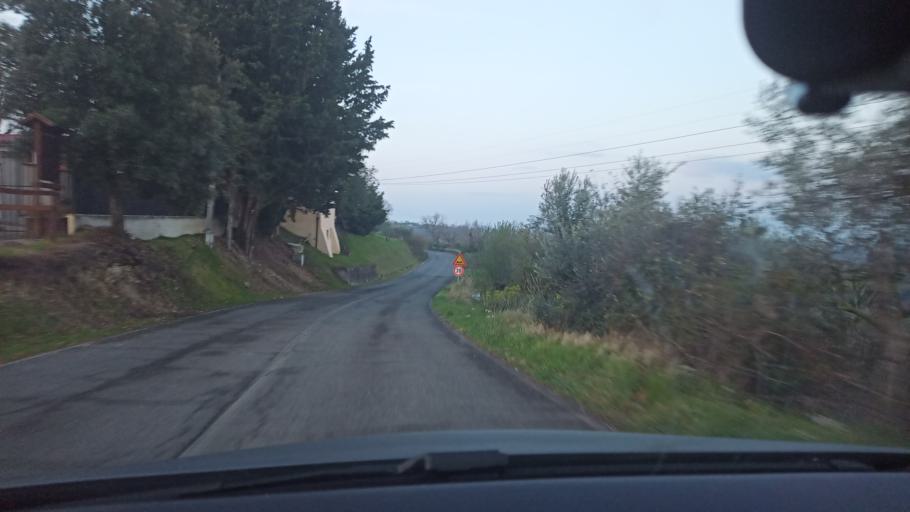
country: IT
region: Latium
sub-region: Provincia di Rieti
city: Montasola
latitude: 42.3701
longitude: 12.6768
